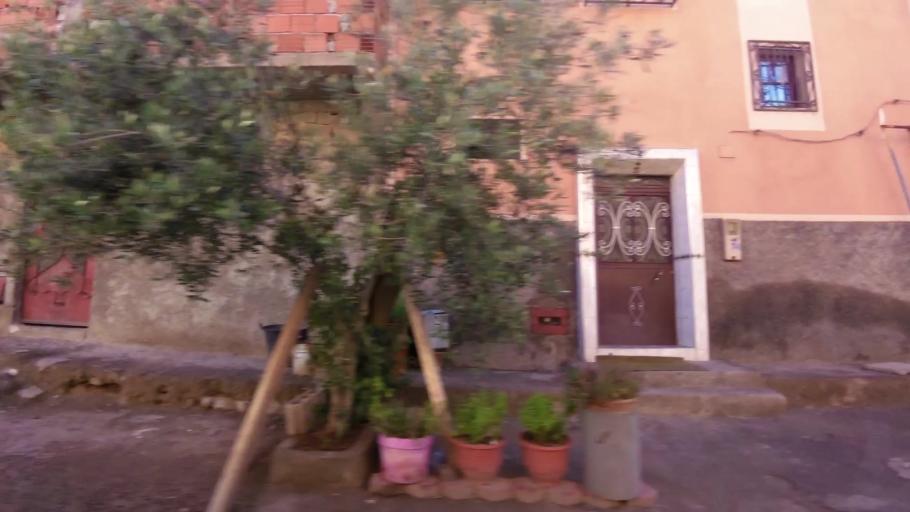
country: MA
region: Marrakech-Tensift-Al Haouz
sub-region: Marrakech
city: Marrakesh
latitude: 31.5945
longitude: -8.0248
